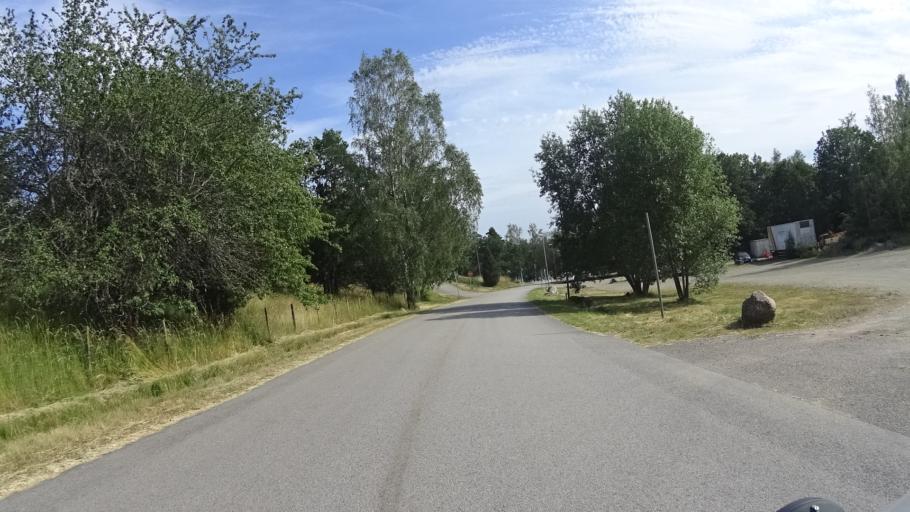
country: SE
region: Kalmar
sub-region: Vasterviks Kommun
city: Gamleby
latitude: 57.8864
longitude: 16.4125
